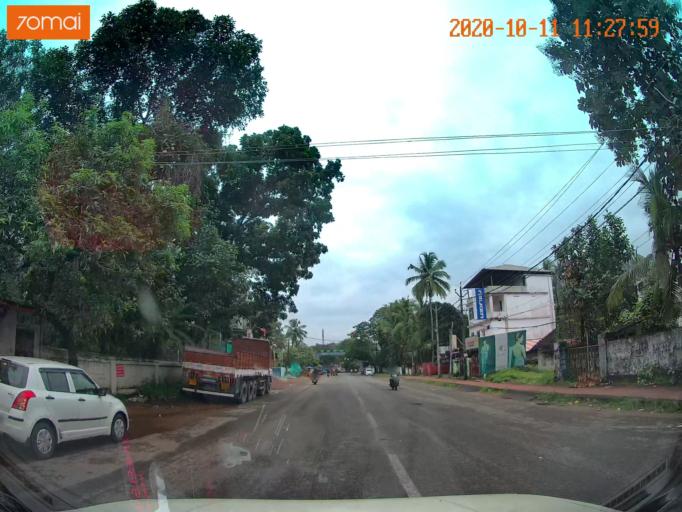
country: IN
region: Kerala
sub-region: Kottayam
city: Changanacheri
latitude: 9.4564
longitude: 76.5519
